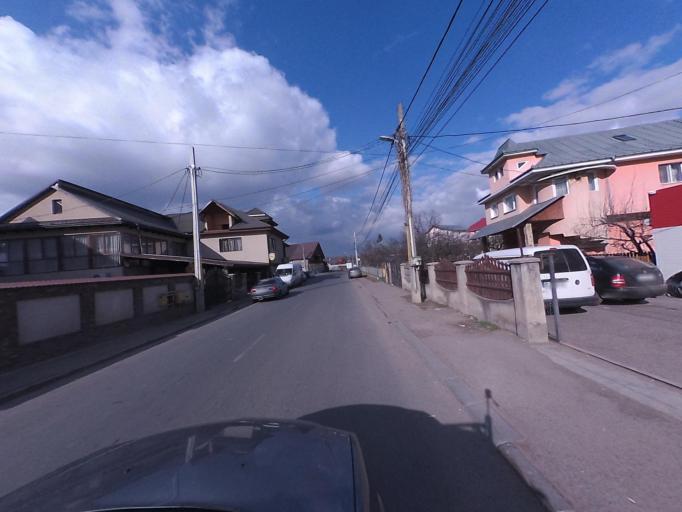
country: RO
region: Neamt
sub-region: Oras Targu Neamt
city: Targu Neamt
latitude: 47.2039
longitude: 26.3733
